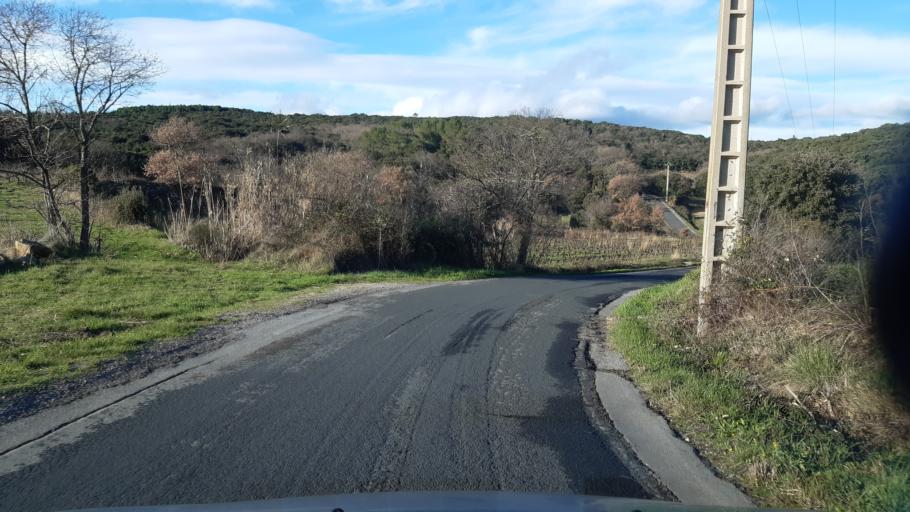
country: FR
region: Languedoc-Roussillon
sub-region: Departement de l'Herault
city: Murviel-les-Montpellier
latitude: 43.6140
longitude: 3.7419
